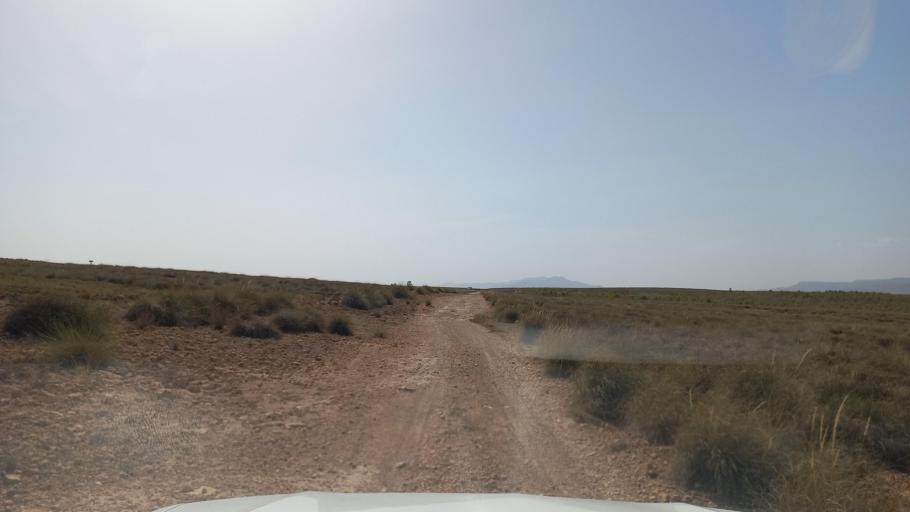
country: TN
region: Al Qasrayn
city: Kasserine
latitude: 35.2153
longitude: 8.9855
